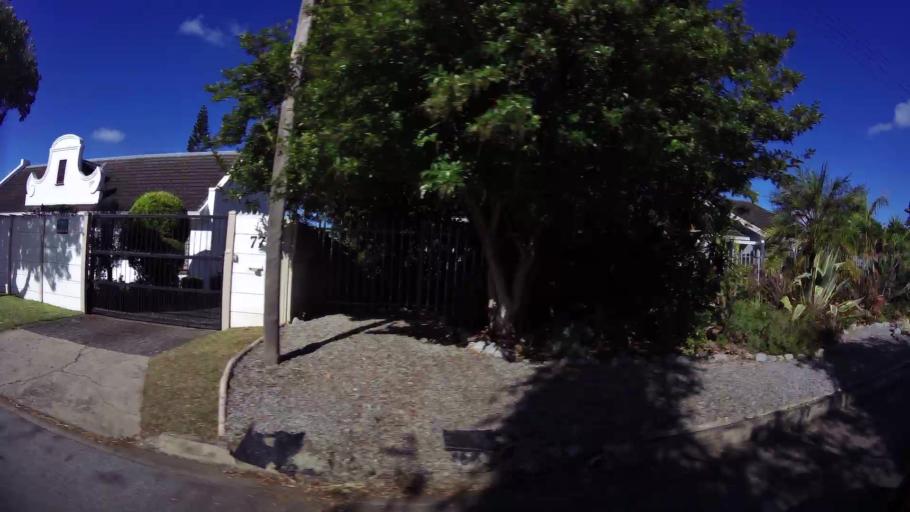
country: ZA
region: Western Cape
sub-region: Eden District Municipality
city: George
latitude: -33.9579
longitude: 22.4339
